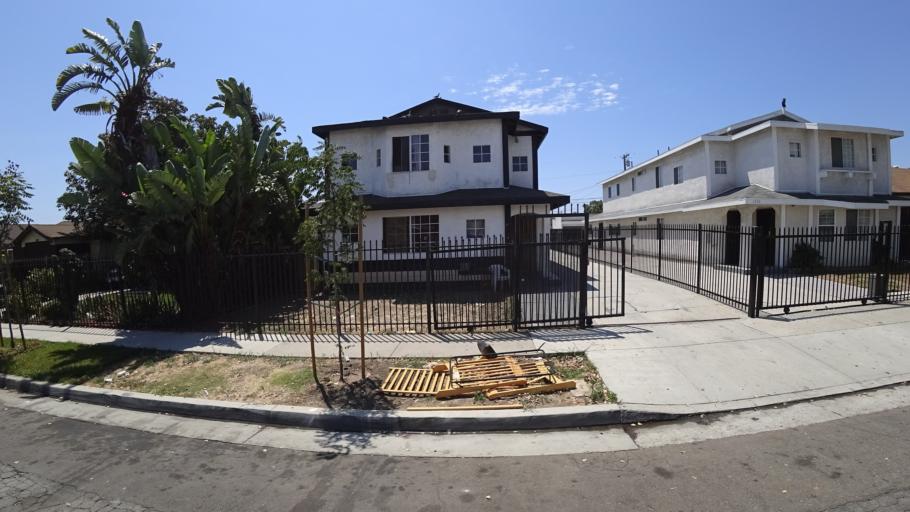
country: US
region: California
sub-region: Los Angeles County
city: Westmont
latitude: 33.9550
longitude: -118.2989
